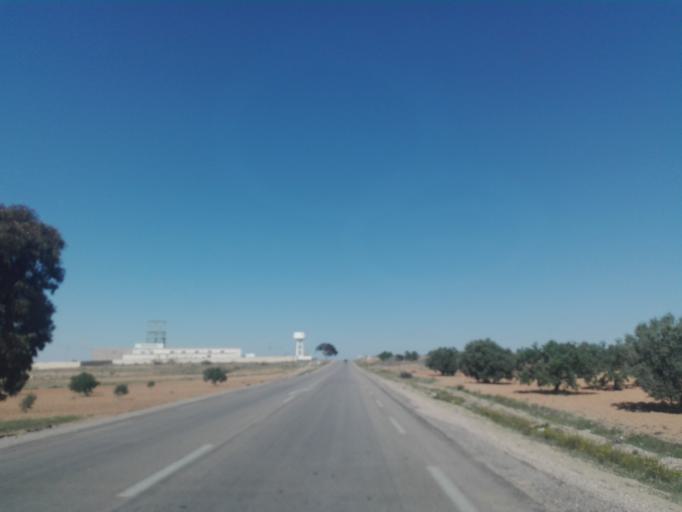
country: TN
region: Safaqis
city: Bi'r `Ali Bin Khalifah
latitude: 34.7395
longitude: 10.3981
